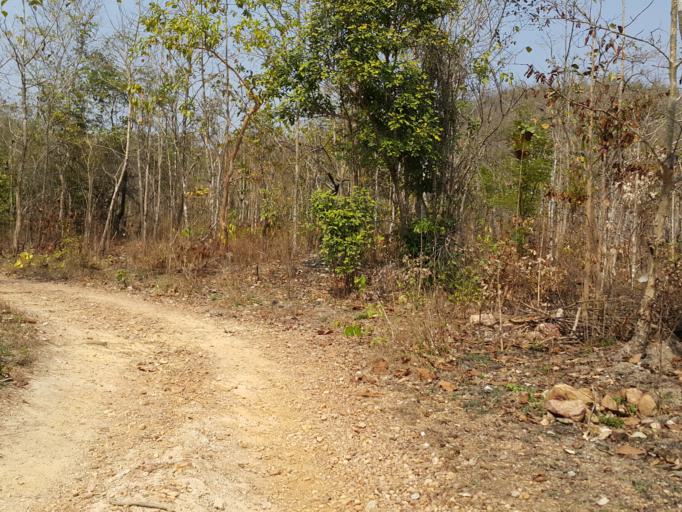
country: TH
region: Sukhothai
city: Thung Saliam
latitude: 17.3197
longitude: 99.5015
